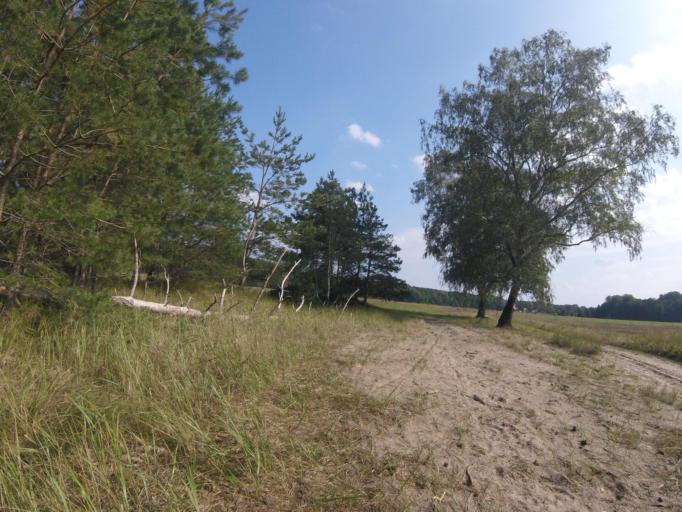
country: DE
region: Brandenburg
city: Bestensee
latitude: 52.2521
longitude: 13.7615
